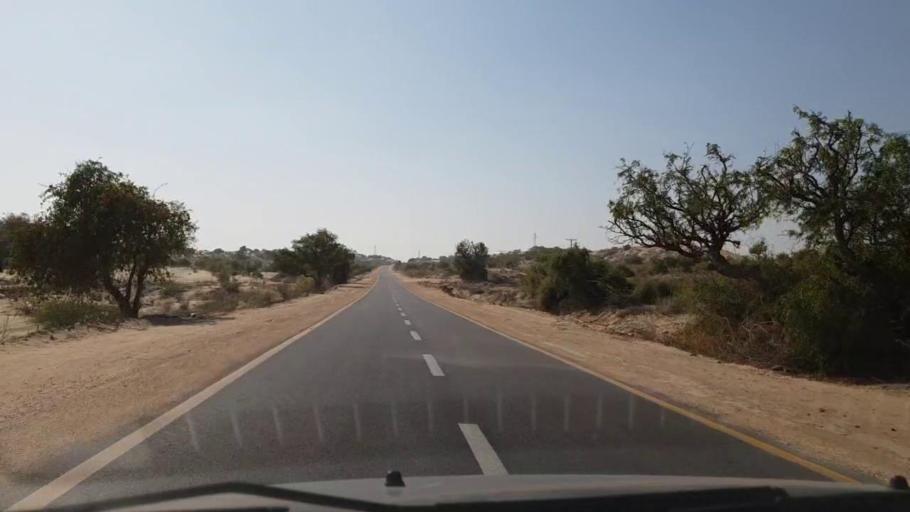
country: PK
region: Sindh
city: Diplo
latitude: 24.4962
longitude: 69.6017
